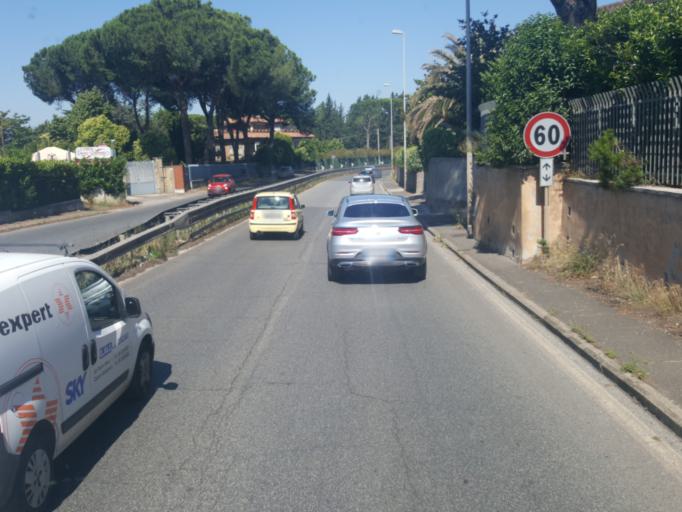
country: IT
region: Latium
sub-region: Citta metropolitana di Roma Capitale
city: Frascati
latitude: 41.8237
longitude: 12.6332
